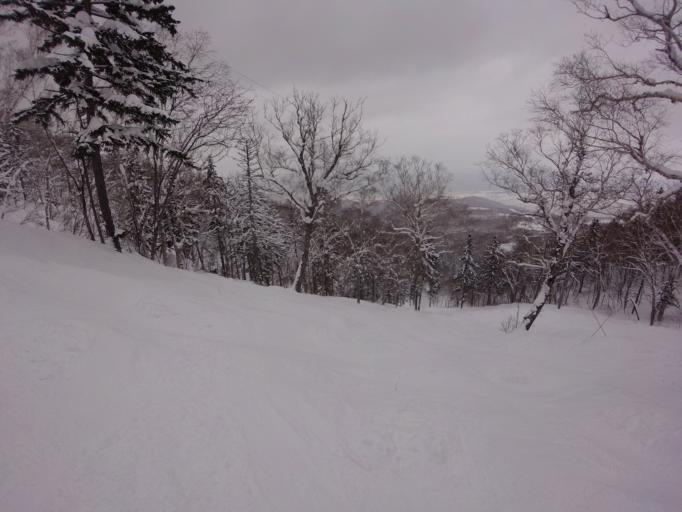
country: JP
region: Hokkaido
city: Sapporo
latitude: 43.0786
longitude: 141.1988
